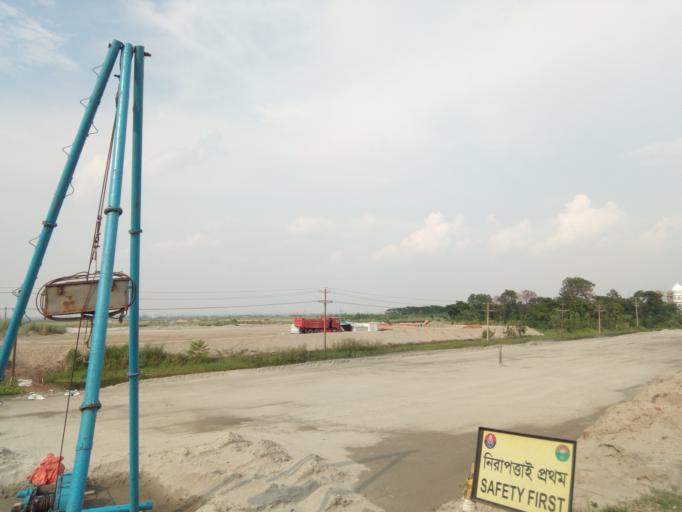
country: BD
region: Dhaka
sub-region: Dhaka
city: Dhaka
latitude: 23.6612
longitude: 90.3686
